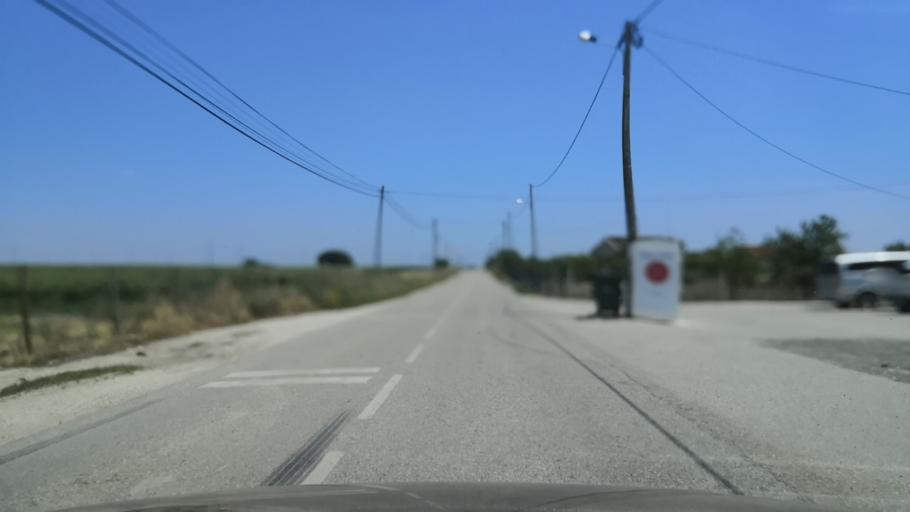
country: PT
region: Setubal
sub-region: Palmela
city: Palmela
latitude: 38.6029
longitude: -8.8144
